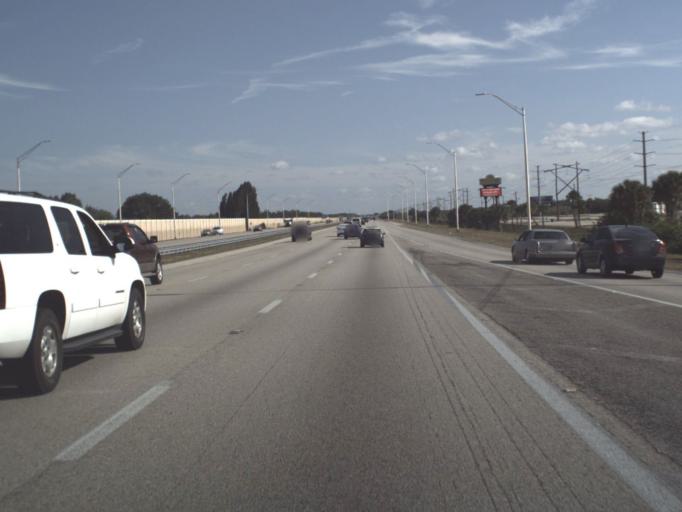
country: US
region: Florida
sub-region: Brevard County
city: June Park
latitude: 28.1177
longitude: -80.7061
